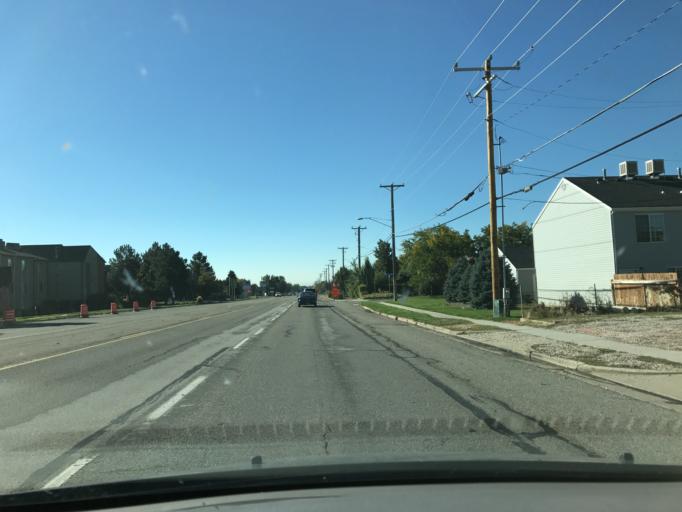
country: US
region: Utah
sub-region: Davis County
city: Hill Air Force Bace
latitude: 41.0858
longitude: -111.9736
